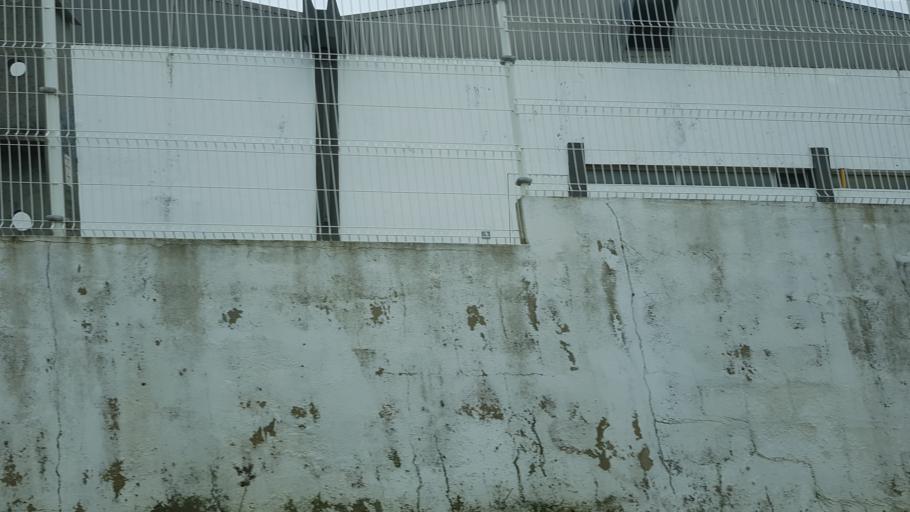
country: PT
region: Lisbon
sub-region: Alenquer
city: Carregado
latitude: 39.0352
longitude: -8.9652
